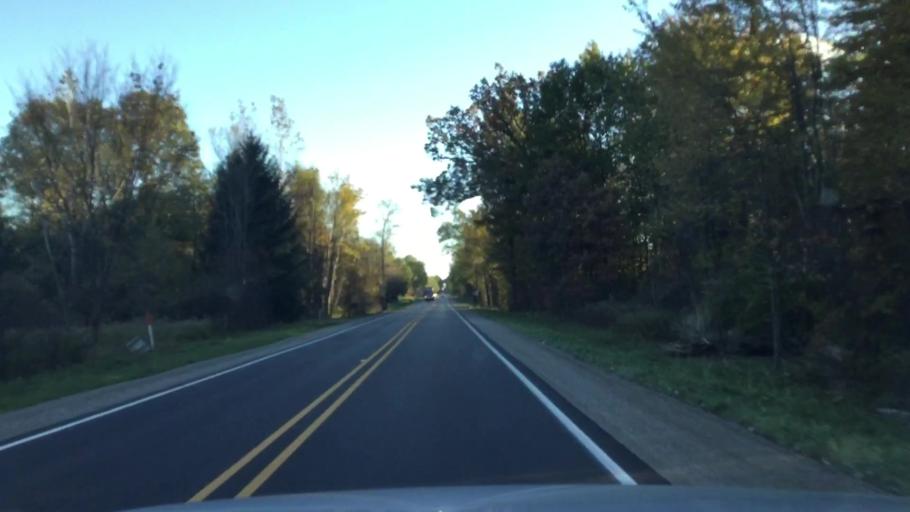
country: US
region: Michigan
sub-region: Lapeer County
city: Almont
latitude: 42.9281
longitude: -83.1439
